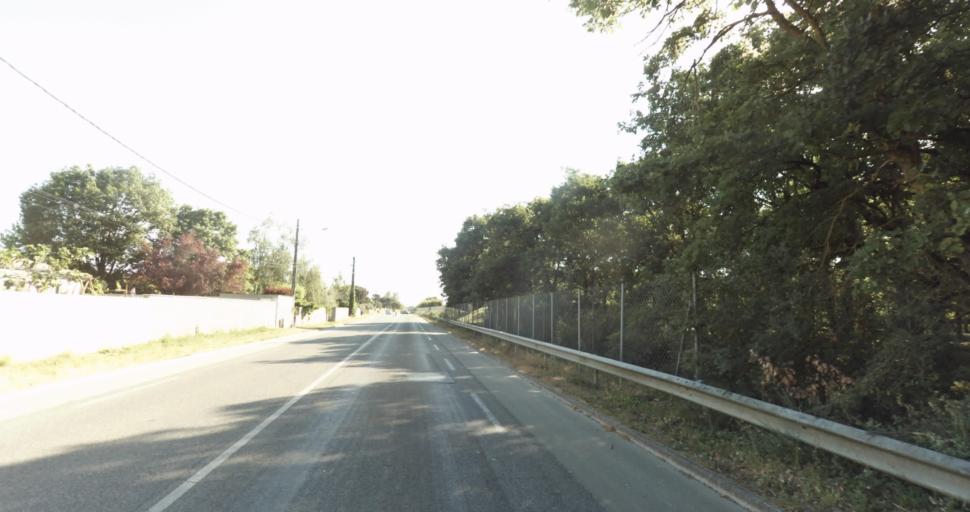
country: FR
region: Midi-Pyrenees
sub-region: Departement de la Haute-Garonne
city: La Salvetat-Saint-Gilles
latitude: 43.5586
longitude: 1.2603
